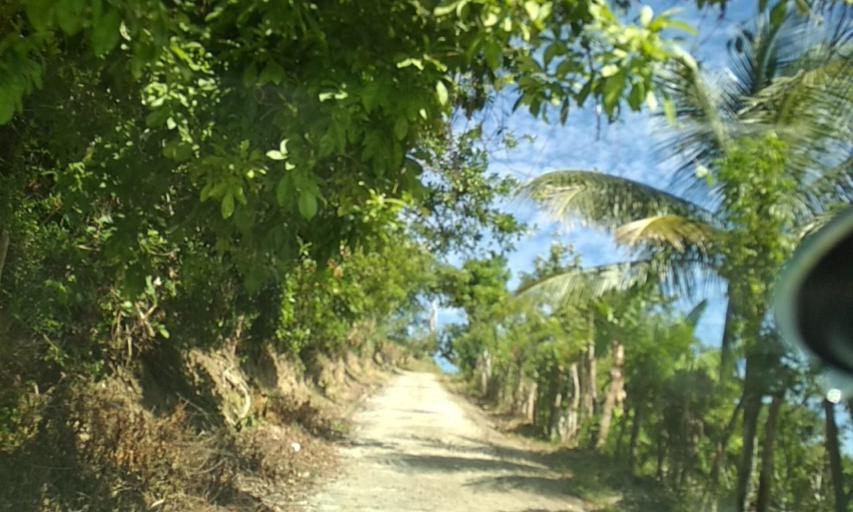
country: MX
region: Veracruz
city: Cazones de Herrera
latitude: 20.6473
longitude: -97.3048
